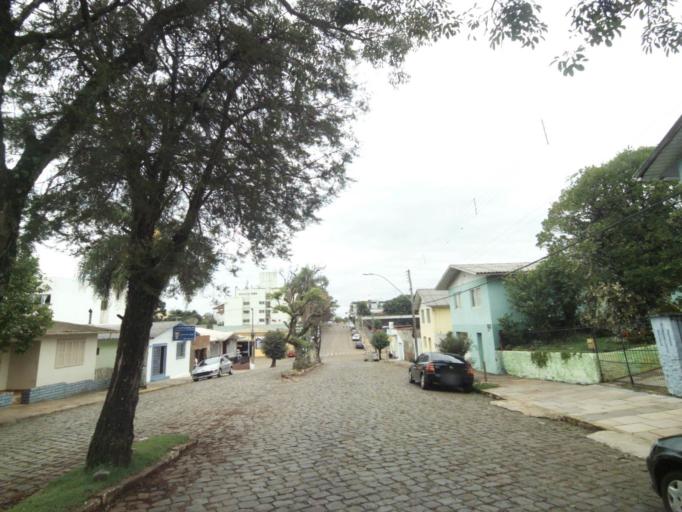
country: BR
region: Rio Grande do Sul
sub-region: Lagoa Vermelha
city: Lagoa Vermelha
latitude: -28.2135
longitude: -51.5245
